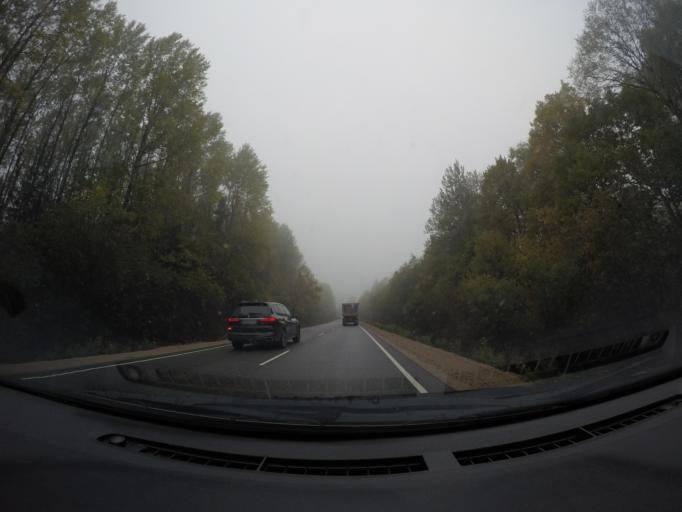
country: RU
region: Moskovskaya
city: Rumyantsevo
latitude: 55.8413
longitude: 36.4696
